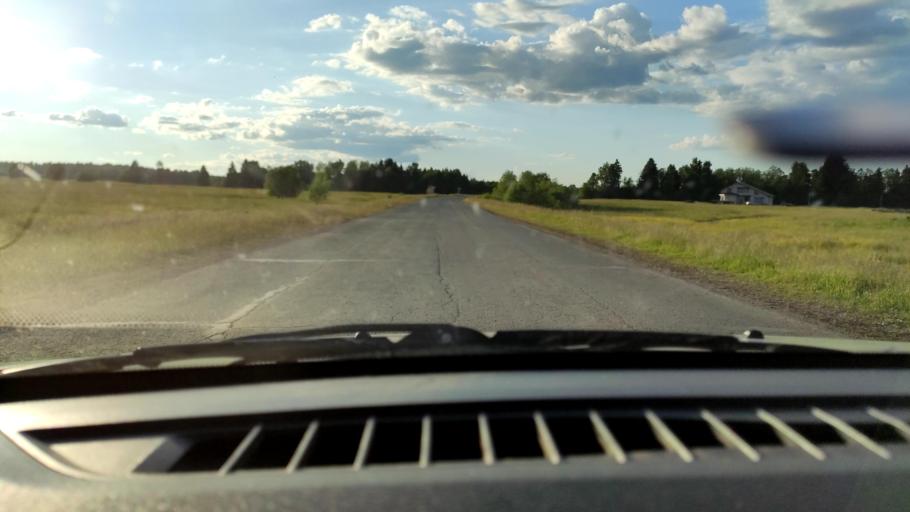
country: RU
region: Perm
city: Uinskoye
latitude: 57.0783
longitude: 56.5557
